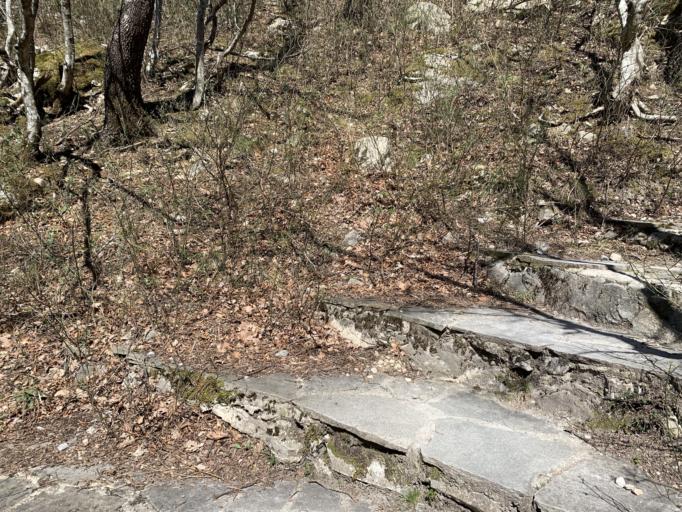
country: GR
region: Central Macedonia
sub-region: Nomos Pellis
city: Loutraki
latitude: 40.9724
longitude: 21.9090
